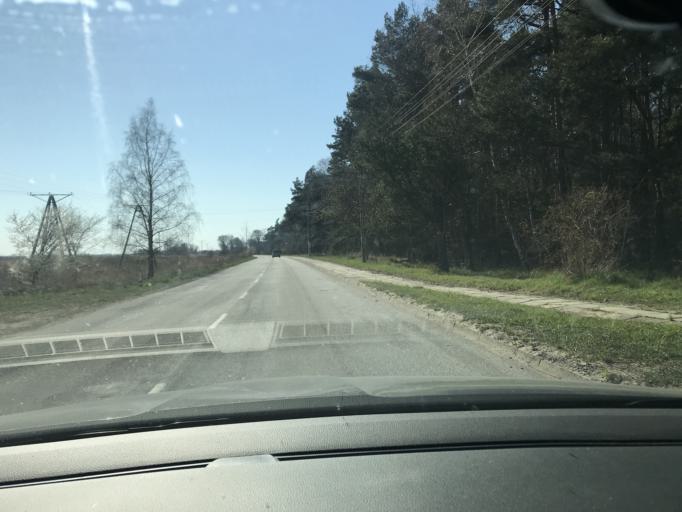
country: PL
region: Pomeranian Voivodeship
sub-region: Powiat nowodworski
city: Sztutowo
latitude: 54.3476
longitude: 19.2612
